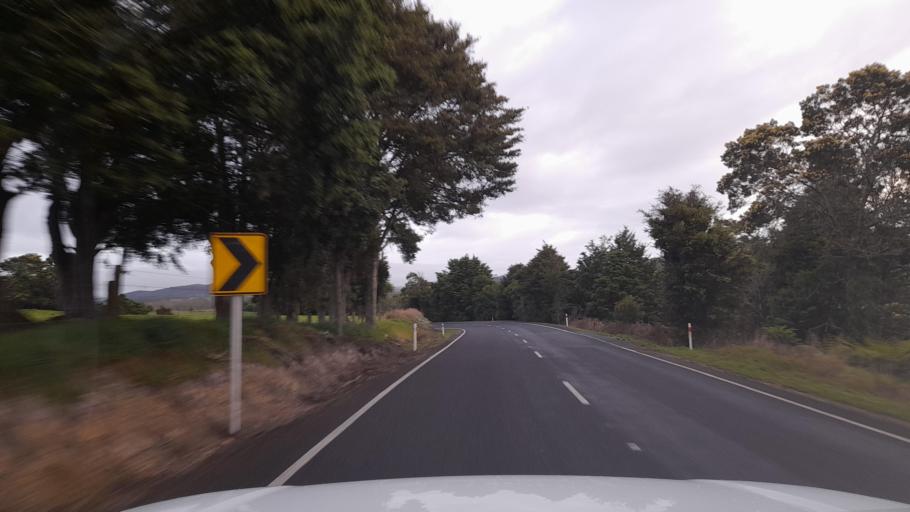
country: NZ
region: Northland
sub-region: Whangarei
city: Maungatapere
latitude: -35.7260
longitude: 174.0431
